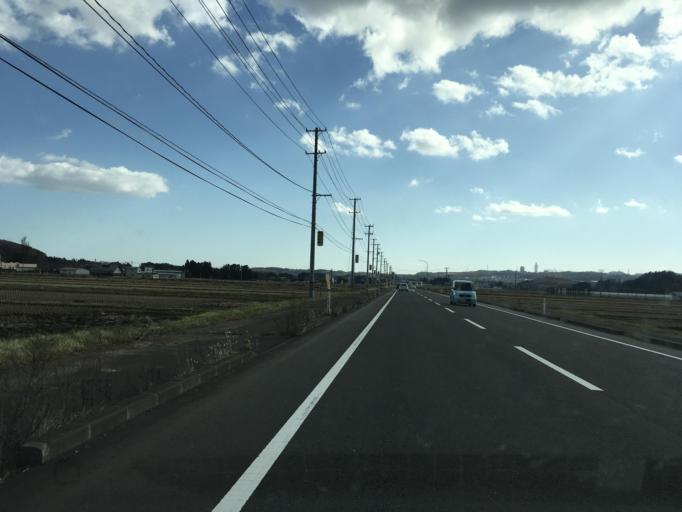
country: JP
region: Miyagi
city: Tomiya
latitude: 38.3422
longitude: 140.7911
